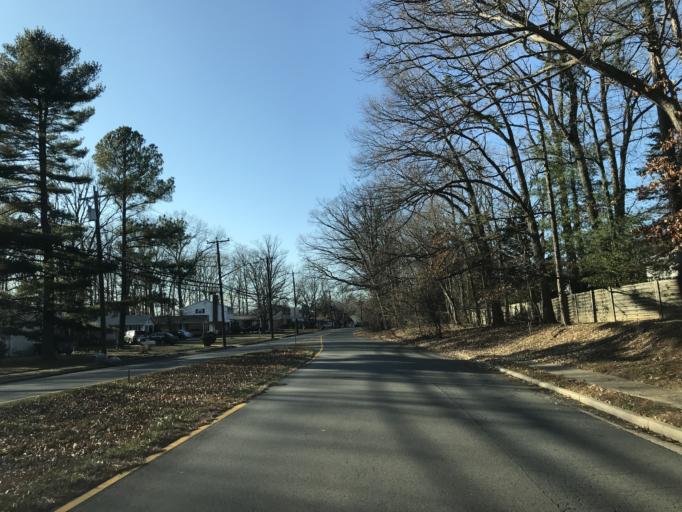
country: US
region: Virginia
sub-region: Fairfax County
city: West Springfield
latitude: 38.7688
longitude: -77.2271
